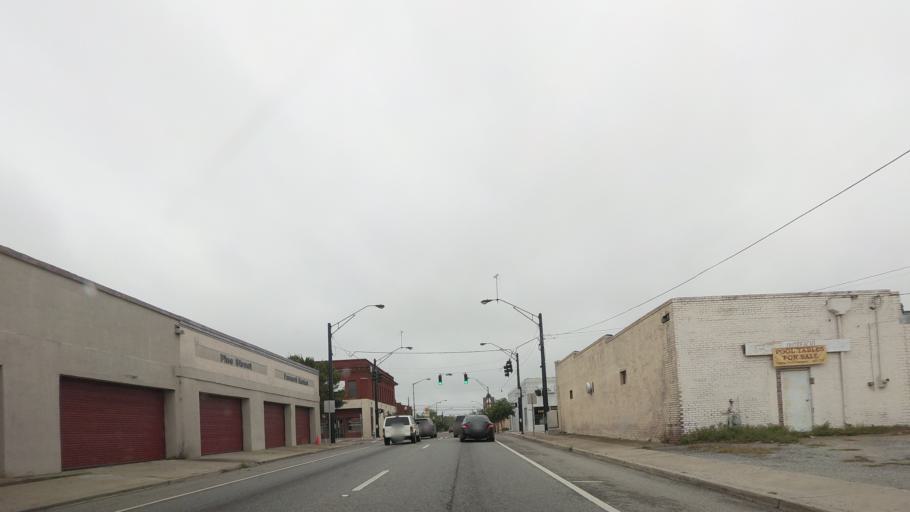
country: US
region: Georgia
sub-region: Ben Hill County
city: Fitzgerald
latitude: 31.7132
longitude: -83.2516
